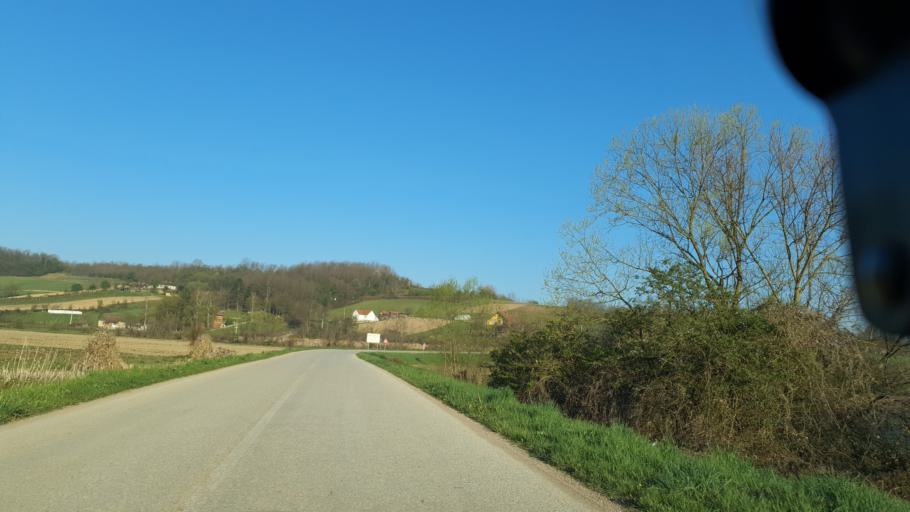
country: RS
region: Central Serbia
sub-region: Kolubarski Okrug
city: Osecina
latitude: 44.3873
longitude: 19.5681
